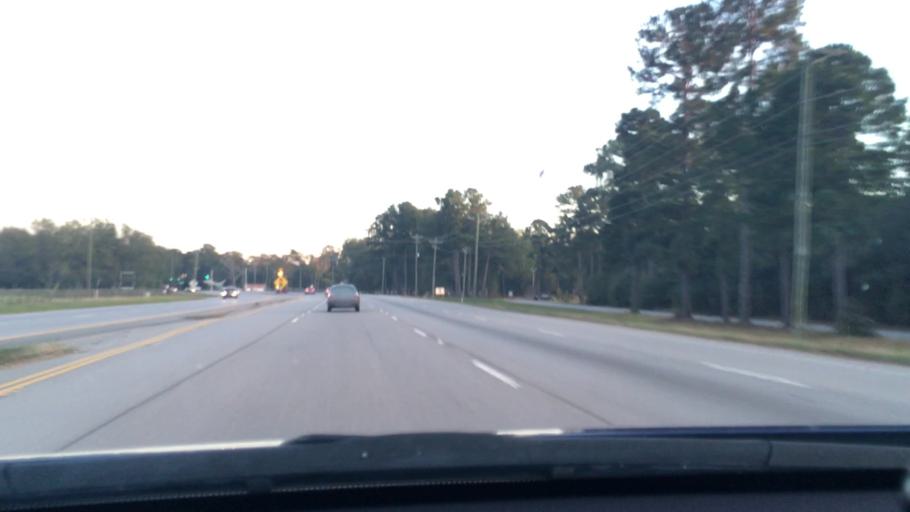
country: US
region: South Carolina
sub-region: Richland County
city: Hopkins
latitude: 33.9428
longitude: -80.8042
